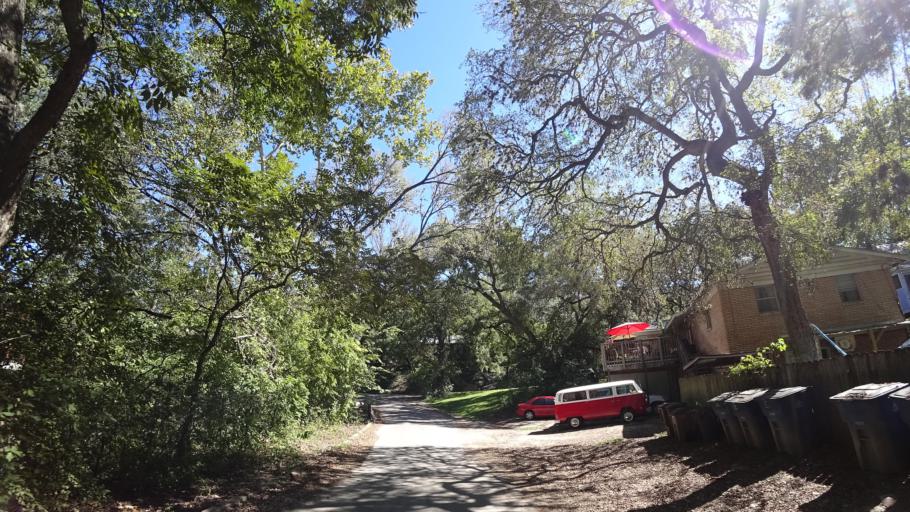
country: US
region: Texas
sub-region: Travis County
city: Austin
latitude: 30.2482
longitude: -97.7425
